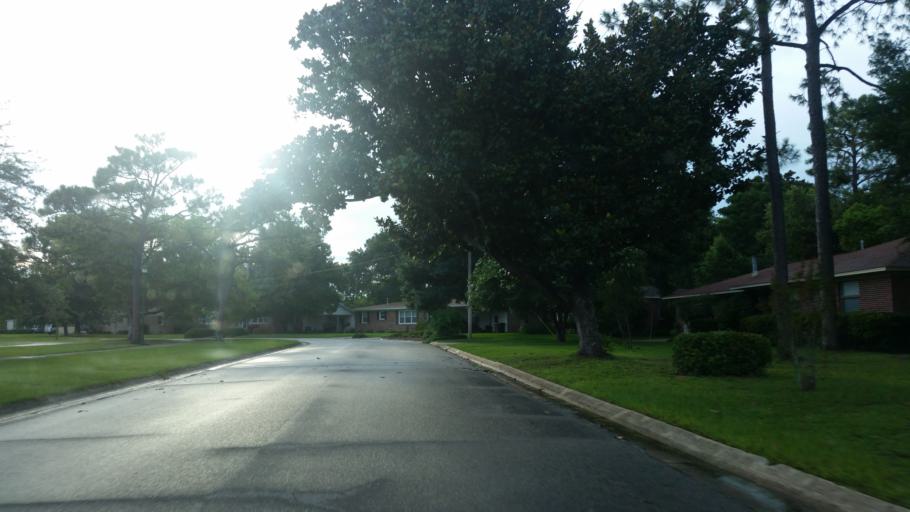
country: US
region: Florida
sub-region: Escambia County
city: Goulding
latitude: 30.4640
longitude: -87.2002
